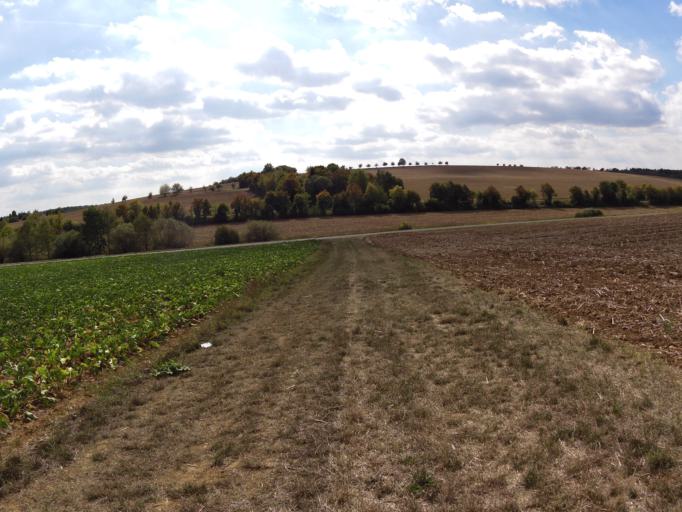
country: DE
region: Bavaria
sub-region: Regierungsbezirk Unterfranken
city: Hettstadt
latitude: 49.7875
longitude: 9.8229
